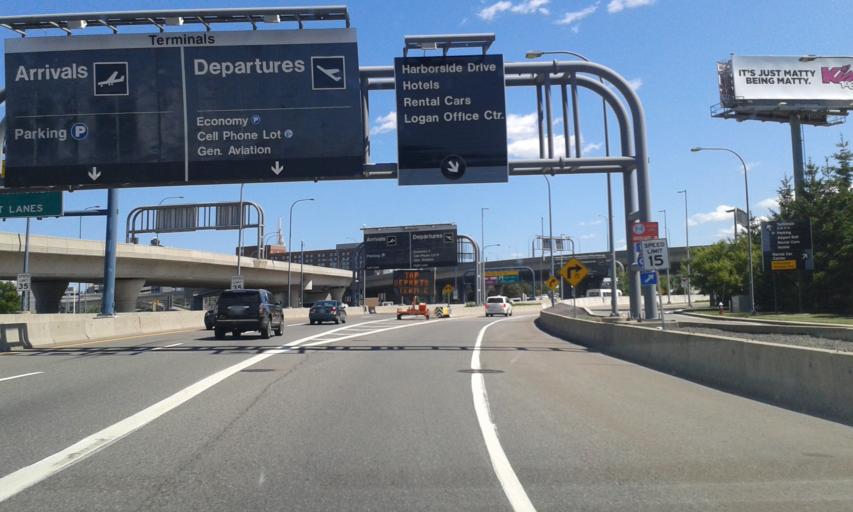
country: US
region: Massachusetts
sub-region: Suffolk County
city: Chelsea
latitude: 42.3711
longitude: -71.0274
